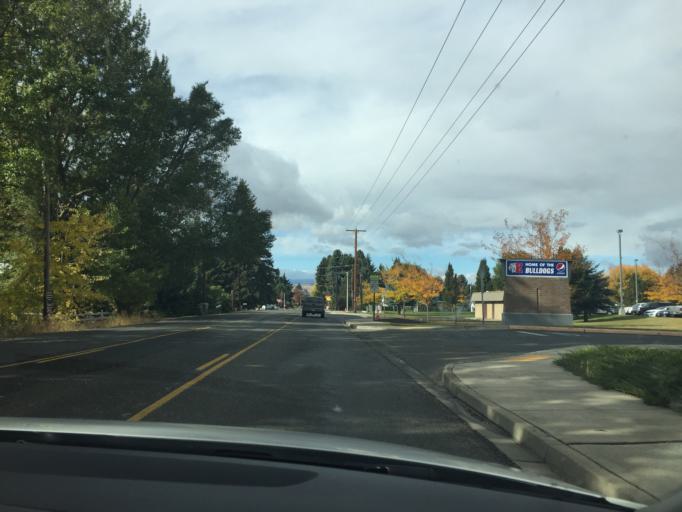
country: US
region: Washington
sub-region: Kittitas County
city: Ellensburg
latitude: 46.9918
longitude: -120.5266
